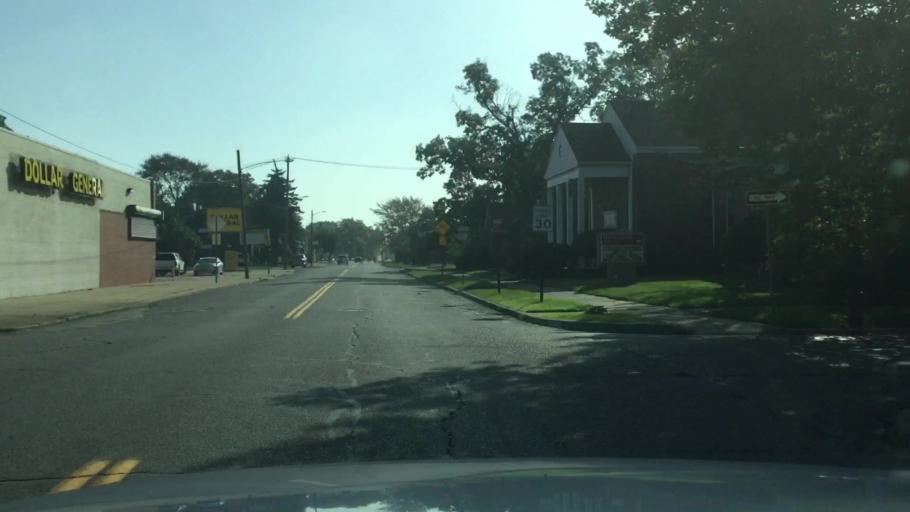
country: US
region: Michigan
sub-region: Oakland County
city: Hazel Park
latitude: 42.4400
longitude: -83.0868
